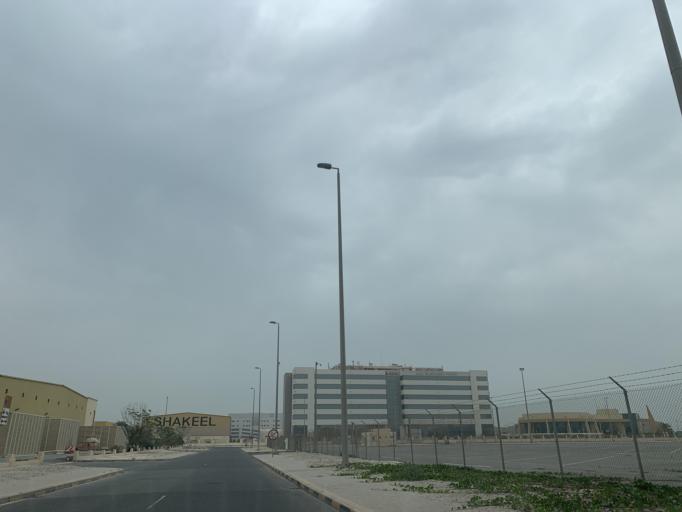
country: BH
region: Muharraq
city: Al Hadd
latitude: 26.2145
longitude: 50.6656
